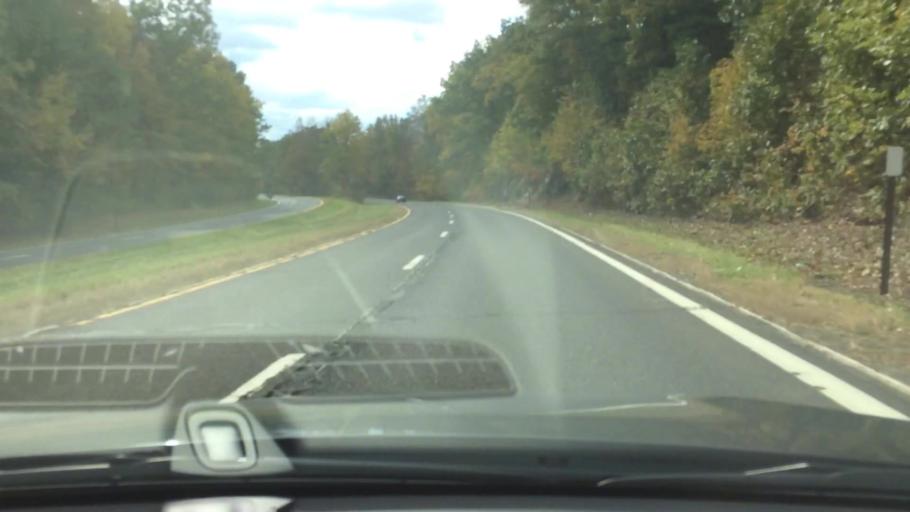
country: US
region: New York
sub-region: Dutchess County
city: Pleasant Valley
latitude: 41.7199
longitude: -73.7837
